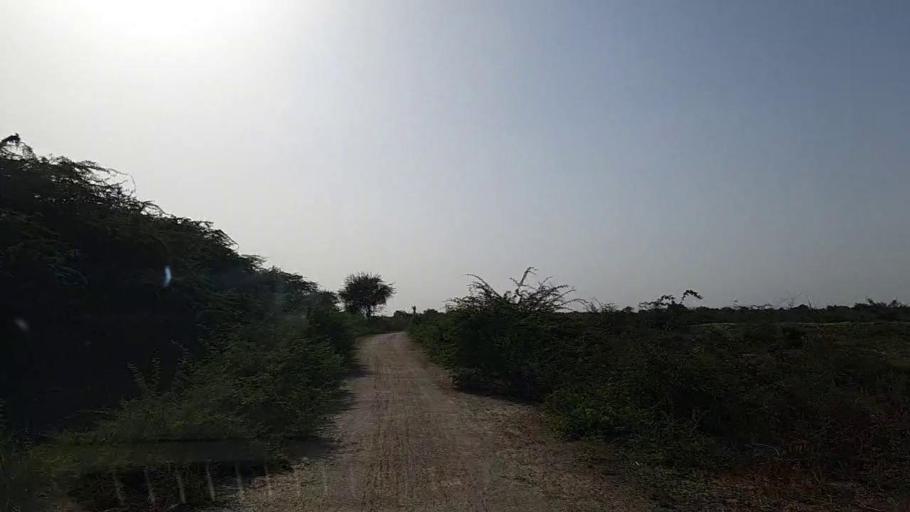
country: PK
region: Sindh
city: Jati
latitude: 24.2885
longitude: 68.2071
